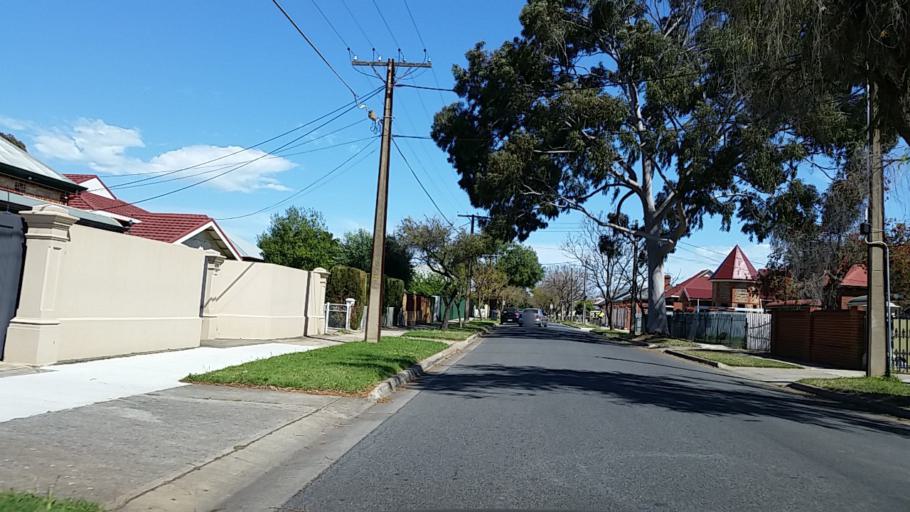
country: AU
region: South Australia
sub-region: Charles Sturt
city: Allenby Gardens
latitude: -34.8994
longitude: 138.5574
